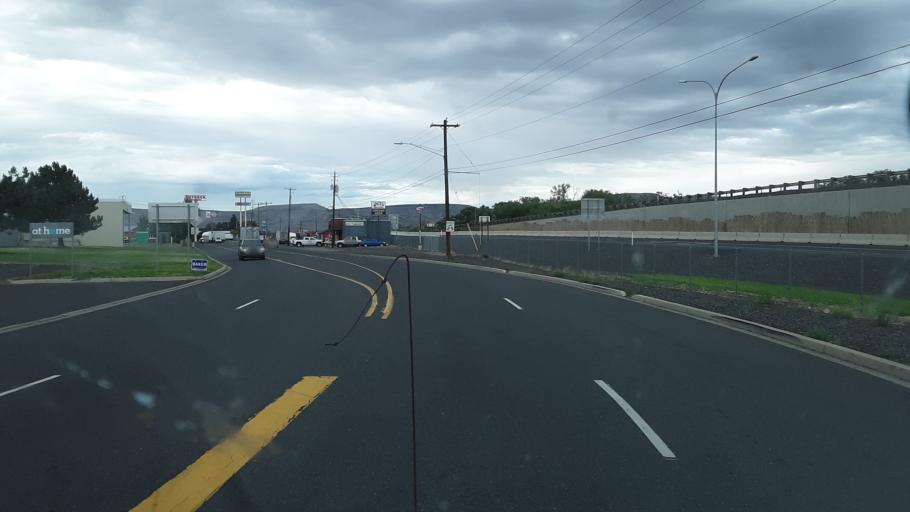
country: US
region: Washington
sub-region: Yakima County
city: Union Gap
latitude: 46.5640
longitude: -120.4733
